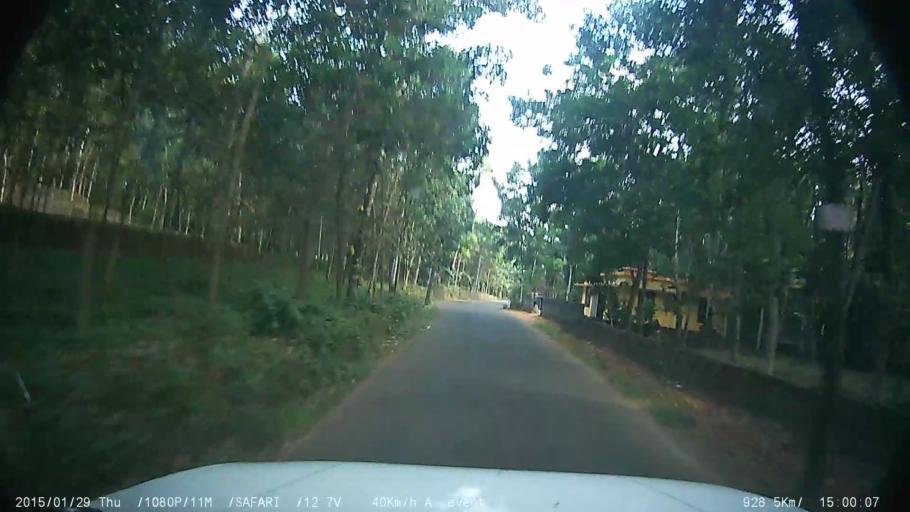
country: IN
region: Kerala
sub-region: Kottayam
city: Palackattumala
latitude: 9.7290
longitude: 76.5645
